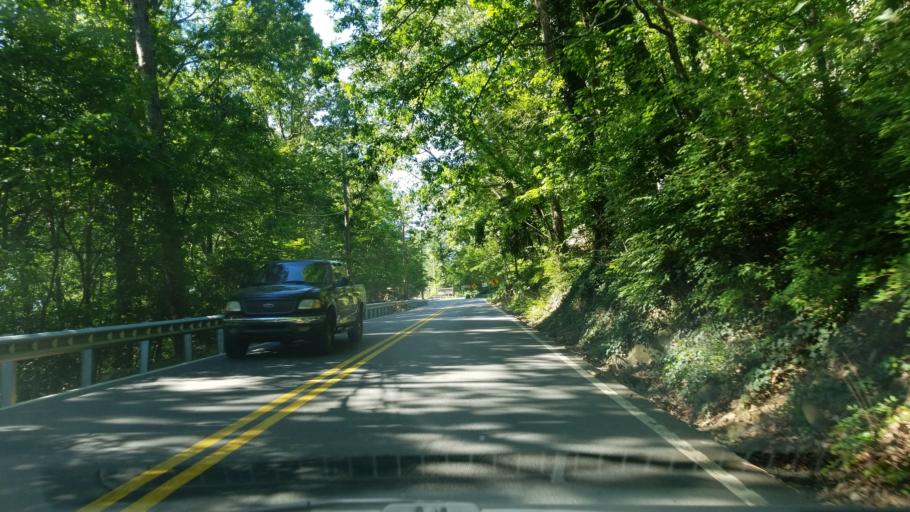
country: US
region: Tennessee
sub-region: Hamilton County
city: Lookout Mountain
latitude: 35.0088
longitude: -85.3377
